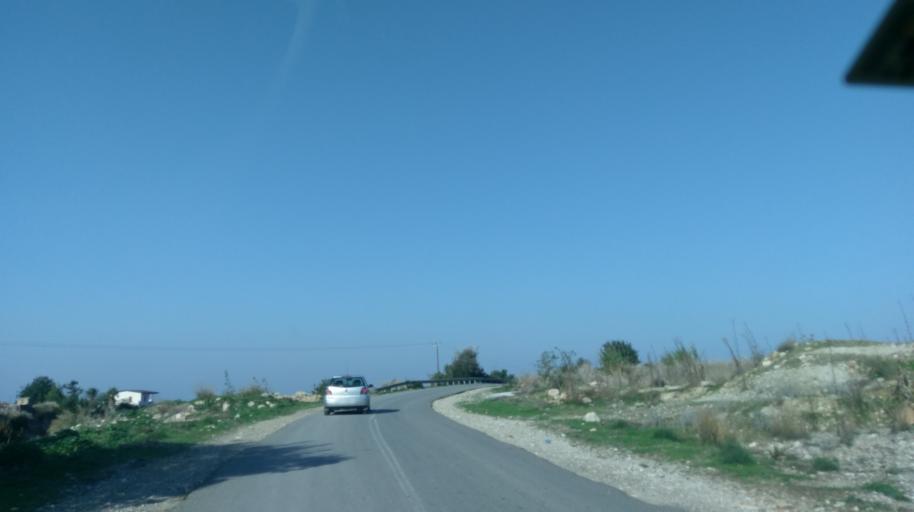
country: CY
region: Ammochostos
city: Leonarisso
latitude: 35.5333
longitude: 34.1921
